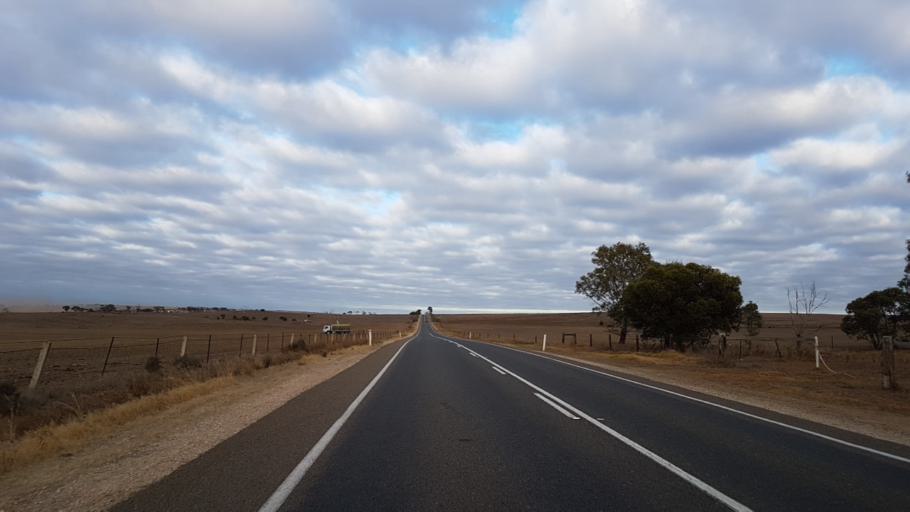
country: AU
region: South Australia
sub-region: Mount Barker
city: Callington
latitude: -35.1870
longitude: 138.9974
